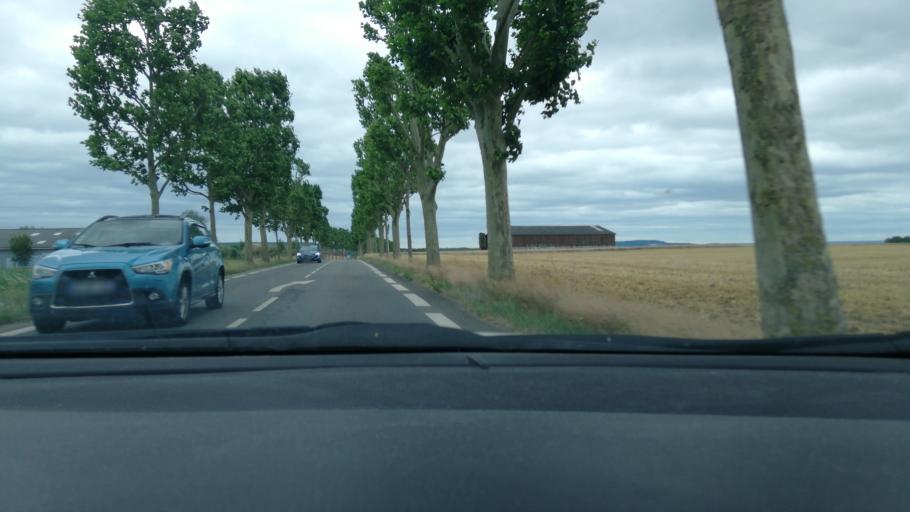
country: FR
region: Ile-de-France
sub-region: Departement du Val-d'Oise
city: Auvers-sur-Oise
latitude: 49.0866
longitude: 2.1500
